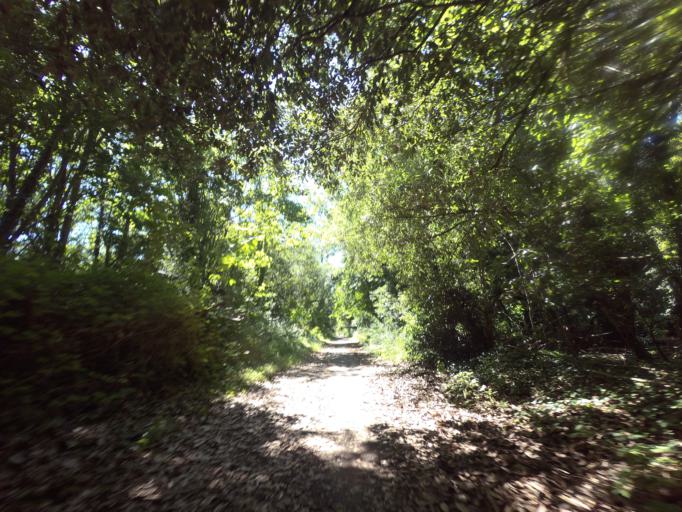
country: GB
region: England
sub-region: Kent
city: Eastry
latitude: 51.2213
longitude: 1.3007
